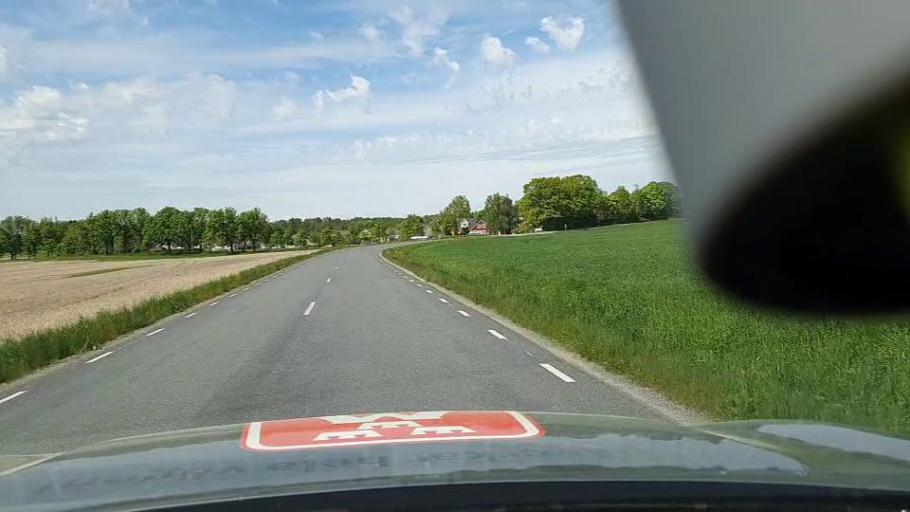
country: SE
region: Soedermanland
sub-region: Eskilstuna Kommun
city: Skogstorp
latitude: 59.3135
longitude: 16.4654
